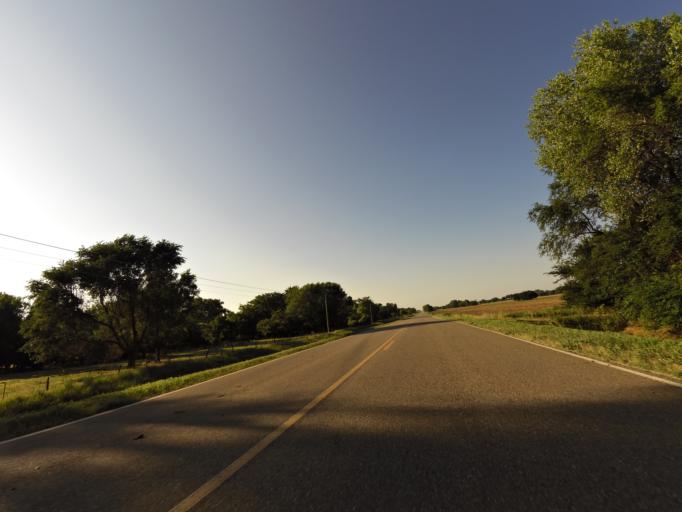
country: US
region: Kansas
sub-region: Reno County
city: Buhler
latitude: 38.1625
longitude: -97.8487
